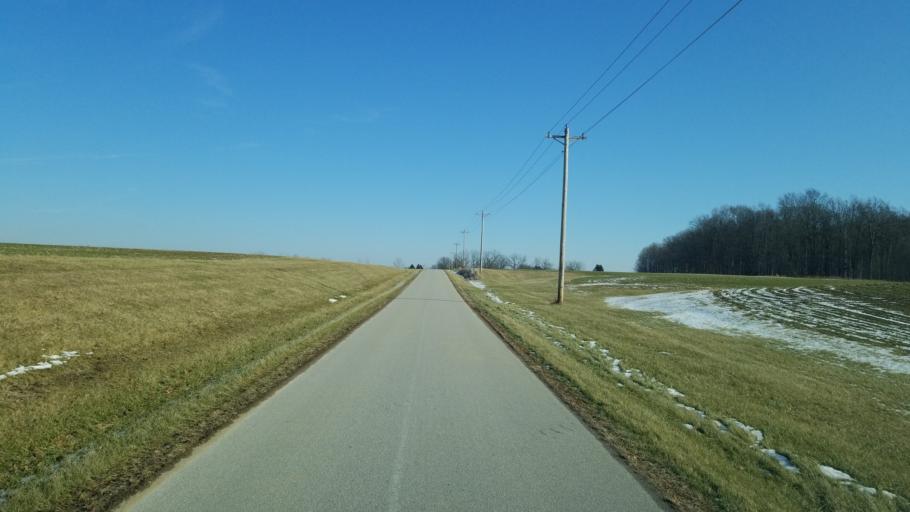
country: US
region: Ohio
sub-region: Huron County
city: Willard
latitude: 41.0902
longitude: -82.6709
